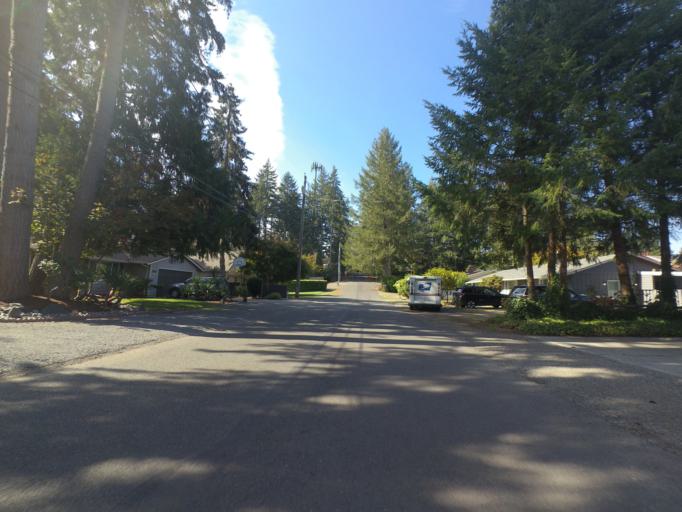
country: US
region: Washington
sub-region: Pierce County
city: University Place
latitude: 47.2158
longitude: -122.5354
